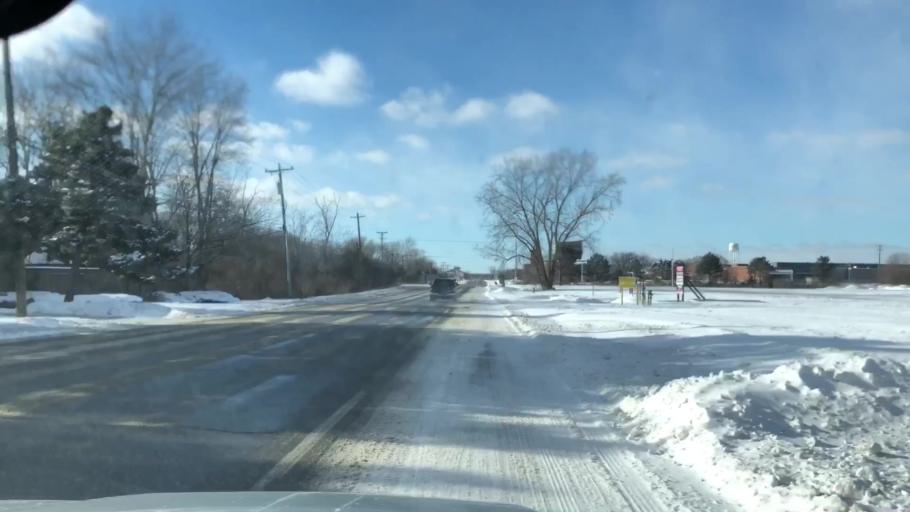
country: US
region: Michigan
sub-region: Wayne County
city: Plymouth
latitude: 42.3724
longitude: -83.4338
